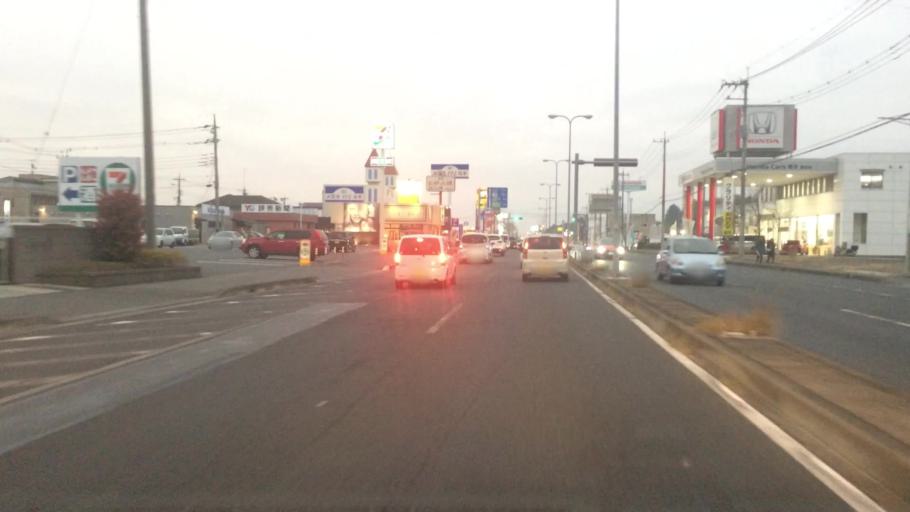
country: JP
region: Tochigi
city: Utsunomiya-shi
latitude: 36.5617
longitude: 139.8508
